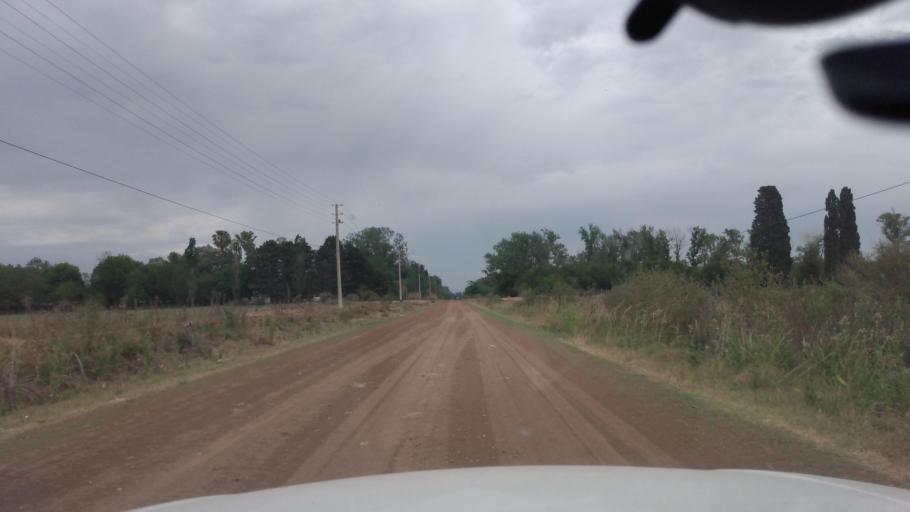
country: AR
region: Buenos Aires
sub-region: Partido de Lujan
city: Lujan
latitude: -34.5552
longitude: -59.1775
